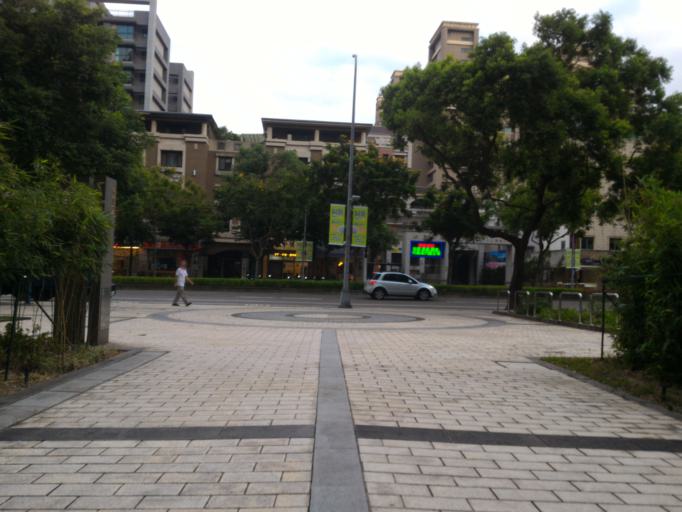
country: TW
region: Taiwan
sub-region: Taoyuan
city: Taoyuan
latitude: 24.9455
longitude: 121.3793
